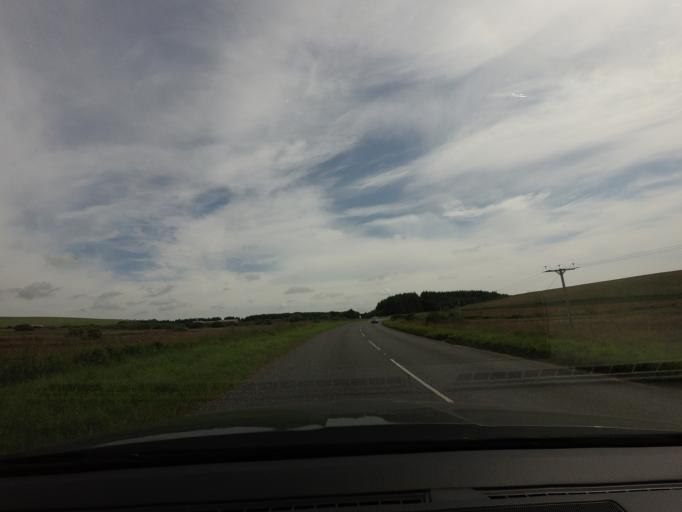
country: GB
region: Scotland
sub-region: Aberdeenshire
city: Rosehearty
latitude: 57.6019
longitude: -2.2753
